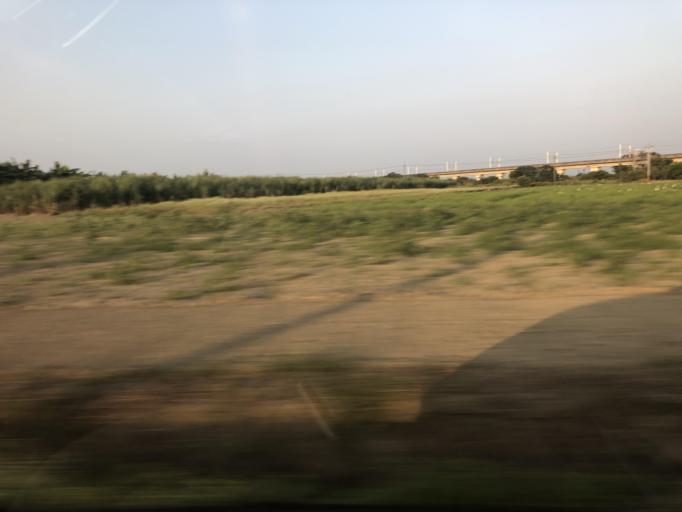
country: TW
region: Taiwan
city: Xinying
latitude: 23.1568
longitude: 120.2749
